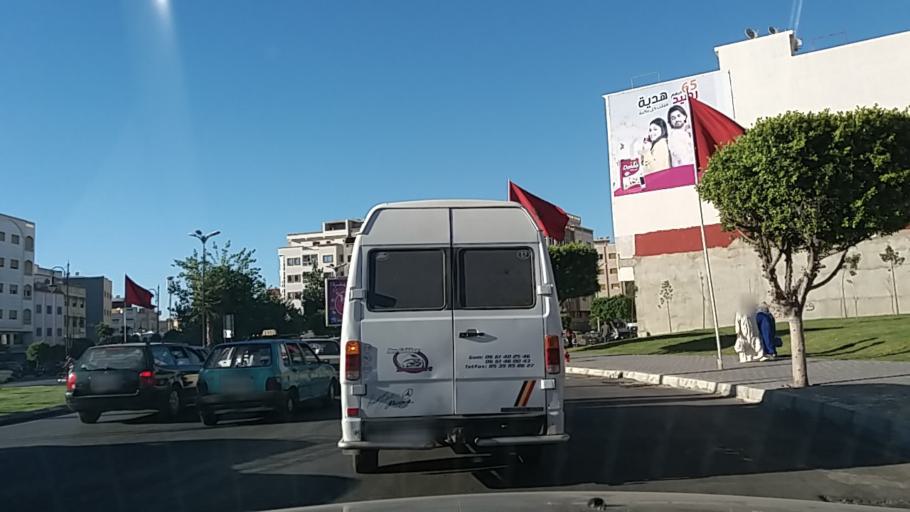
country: MA
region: Tanger-Tetouan
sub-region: Tanger-Assilah
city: Tangier
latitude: 35.7519
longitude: -5.7999
